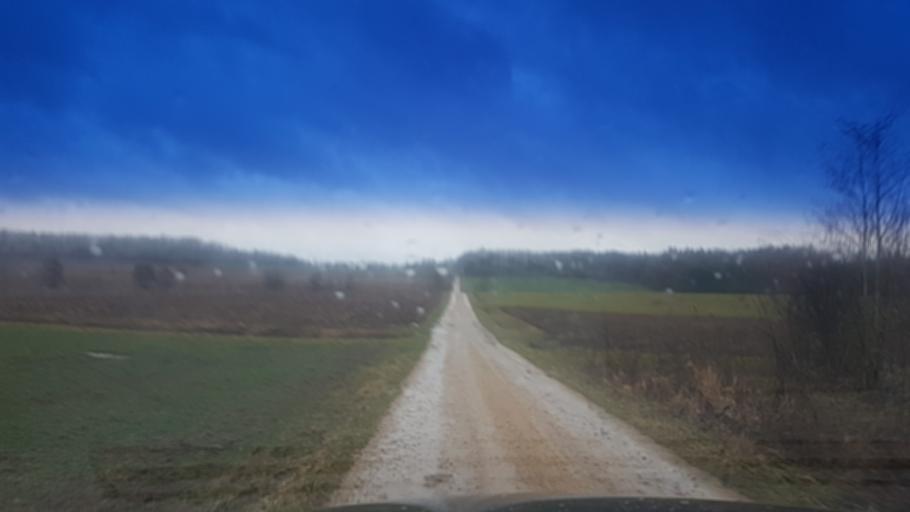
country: DE
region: Bavaria
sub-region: Upper Franconia
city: Zapfendorf
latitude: 49.9976
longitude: 10.9809
